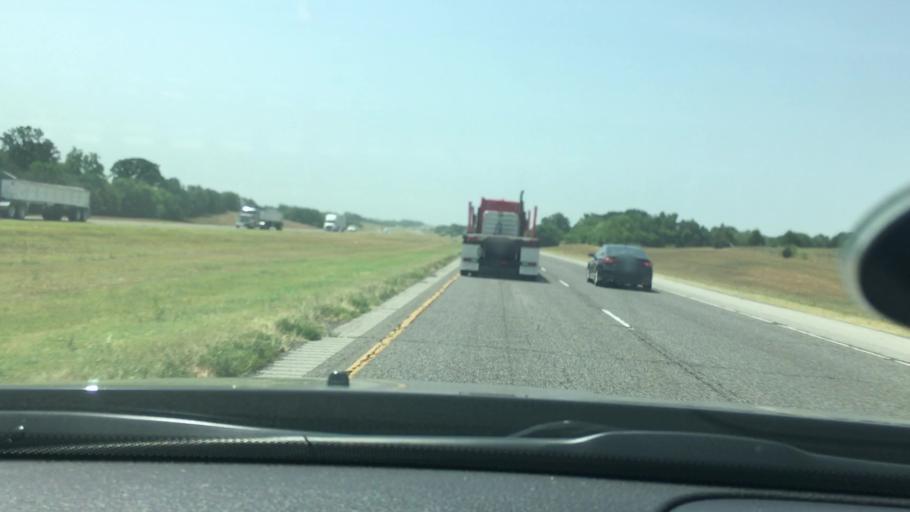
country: US
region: Oklahoma
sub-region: Garvin County
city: Wynnewood
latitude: 34.6000
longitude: -97.2105
